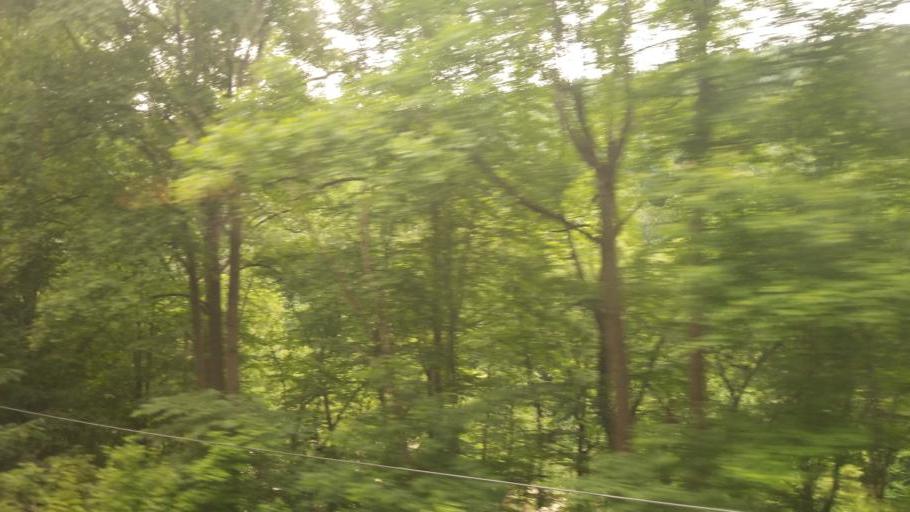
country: US
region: Pennsylvania
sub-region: Fayette County
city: South Connellsville
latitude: 39.9120
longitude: -79.4794
